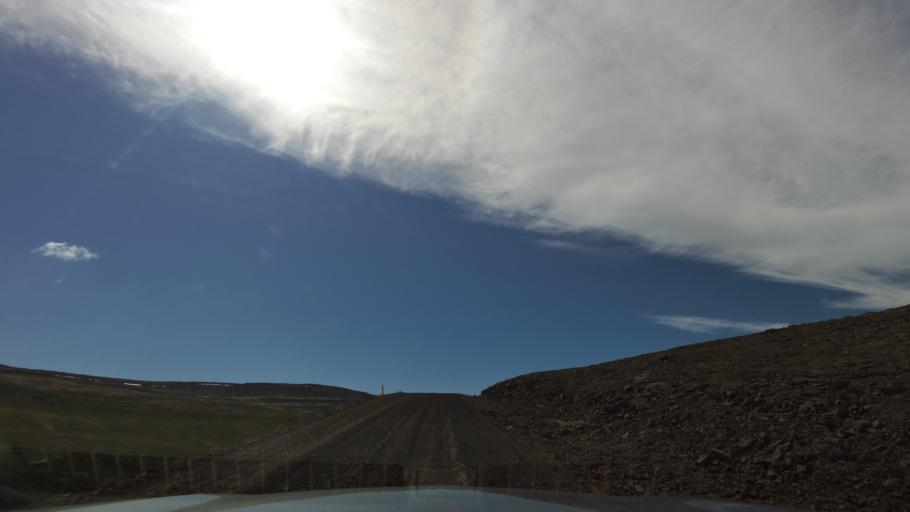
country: IS
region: West
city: Olafsvik
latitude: 65.5223
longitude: -23.9264
